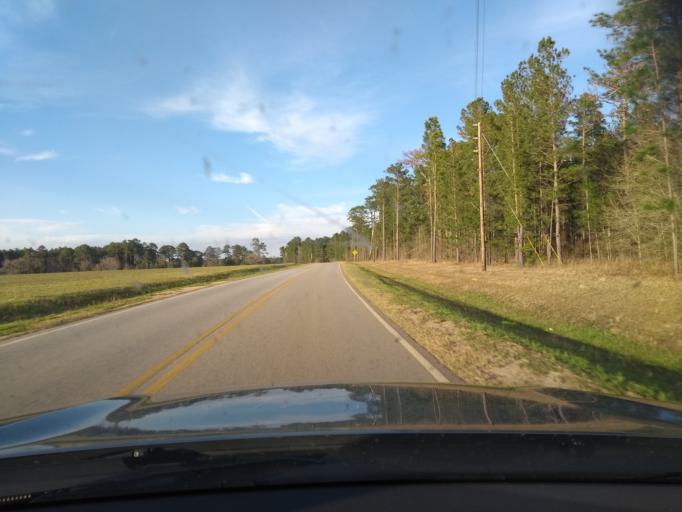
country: US
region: Georgia
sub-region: Bulloch County
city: Statesboro
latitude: 32.3447
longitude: -81.7728
